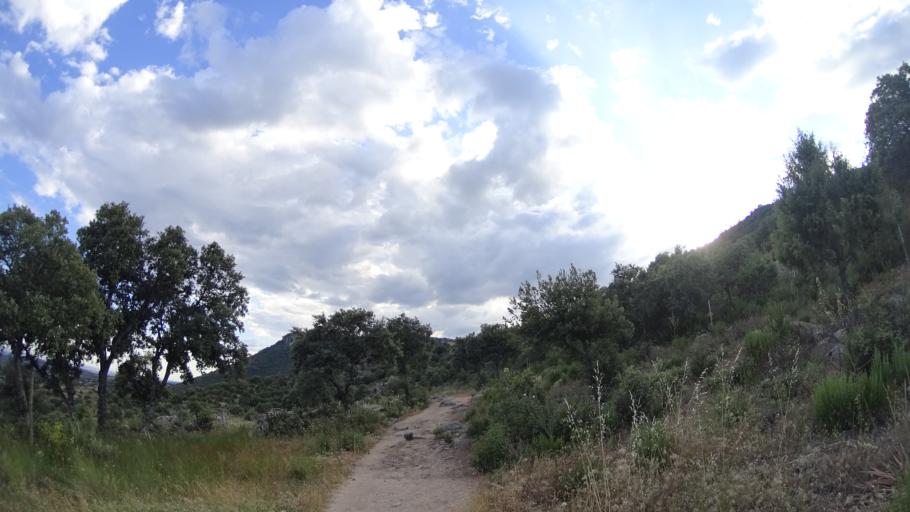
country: ES
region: Madrid
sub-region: Provincia de Madrid
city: Hoyo de Manzanares
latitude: 40.6320
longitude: -3.9113
